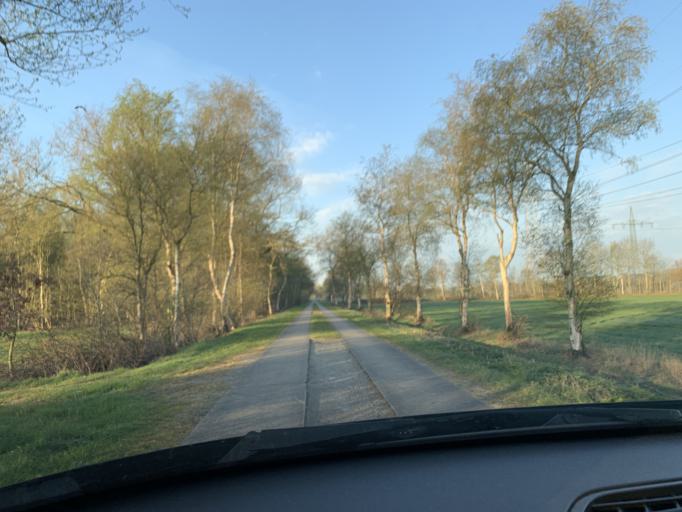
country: DE
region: Lower Saxony
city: Apen
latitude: 53.2841
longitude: 7.8241
